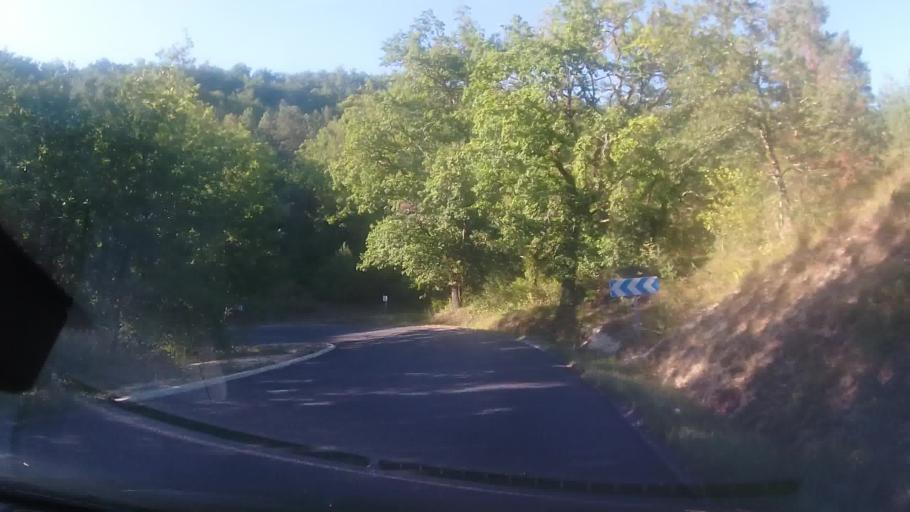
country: FR
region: Aquitaine
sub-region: Departement de la Dordogne
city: Cenac-et-Saint-Julien
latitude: 44.7900
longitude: 1.1835
